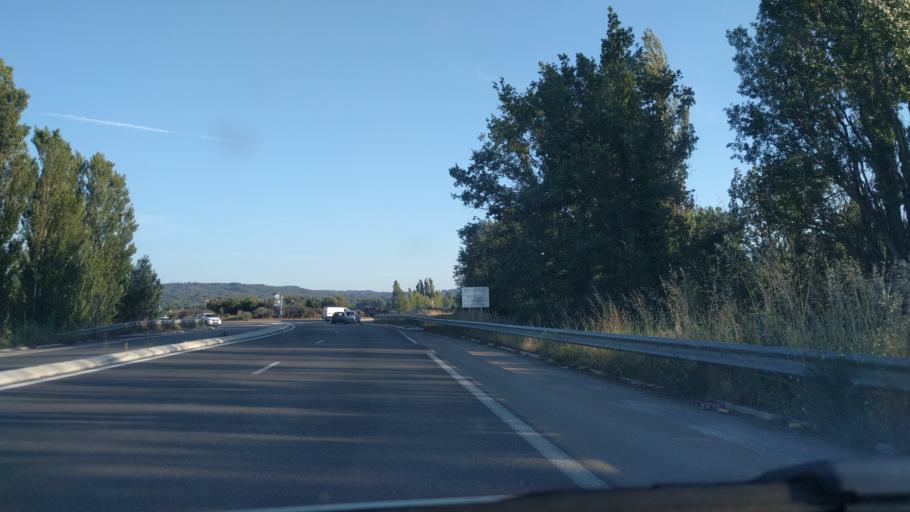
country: FR
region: Provence-Alpes-Cote d'Azur
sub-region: Departement du Vaucluse
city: Pertuis
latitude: 43.6612
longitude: 5.4948
